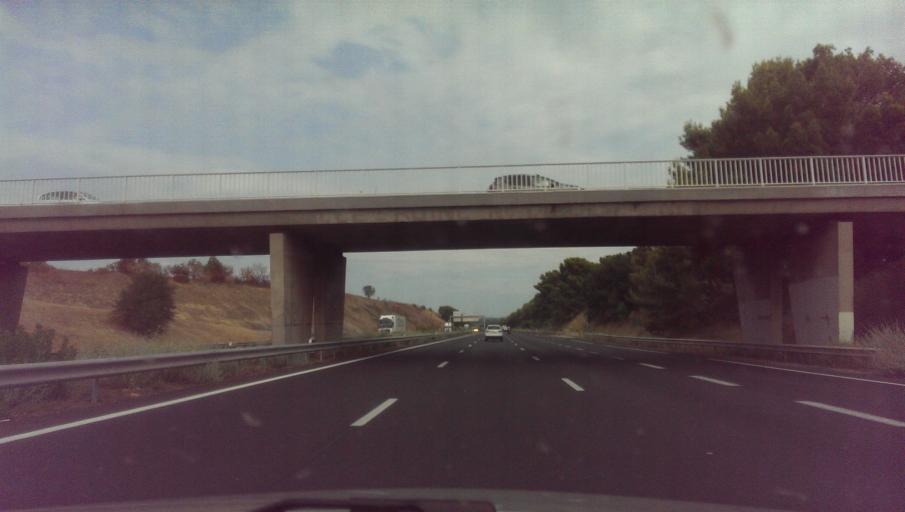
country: FR
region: Languedoc-Roussillon
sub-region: Departement de l'Herault
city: Vendres
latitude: 43.3035
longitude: 3.2227
